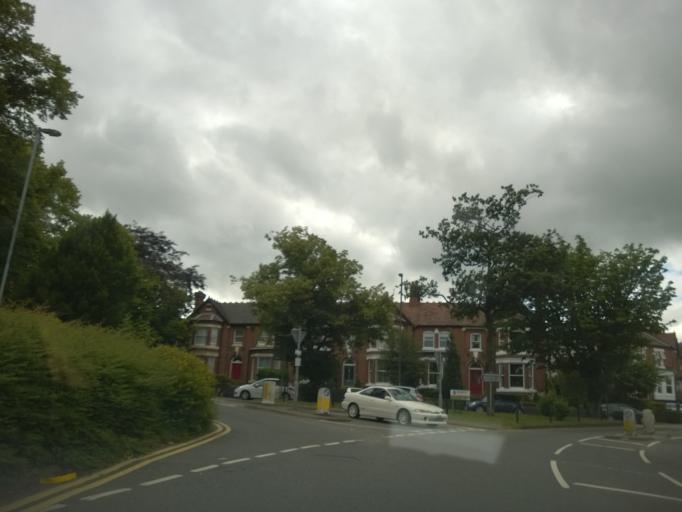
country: GB
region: England
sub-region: Leicestershire
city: Hinckley
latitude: 52.5423
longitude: -1.3631
